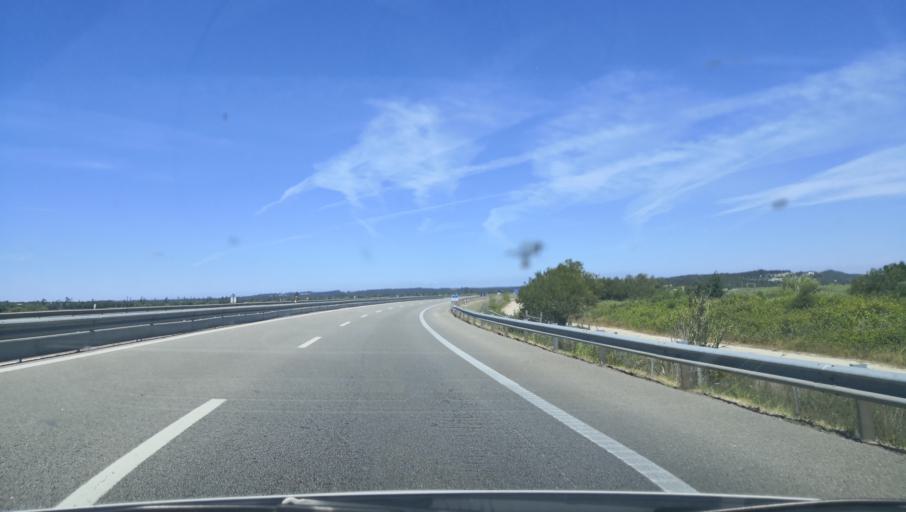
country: PT
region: Coimbra
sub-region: Montemor-O-Velho
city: Montemor-o-Velho
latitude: 40.1570
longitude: -8.7384
